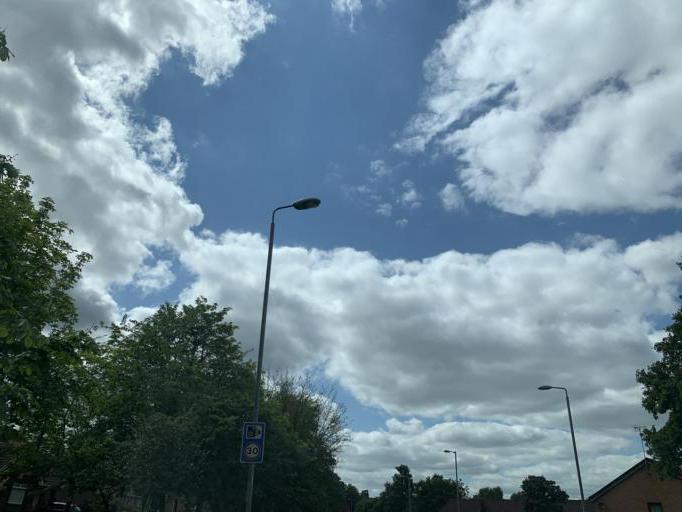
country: GB
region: Scotland
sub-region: East Renfrewshire
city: Newton Mearns
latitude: 55.7789
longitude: -4.3345
